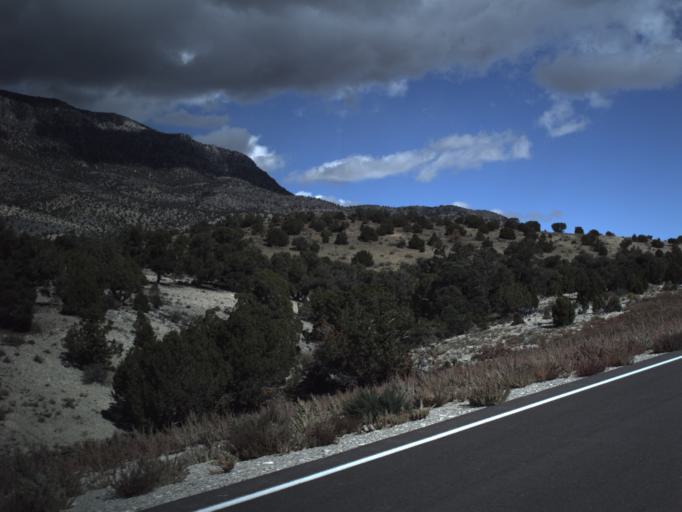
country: US
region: Utah
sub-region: Beaver County
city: Milford
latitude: 38.5159
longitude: -113.5574
